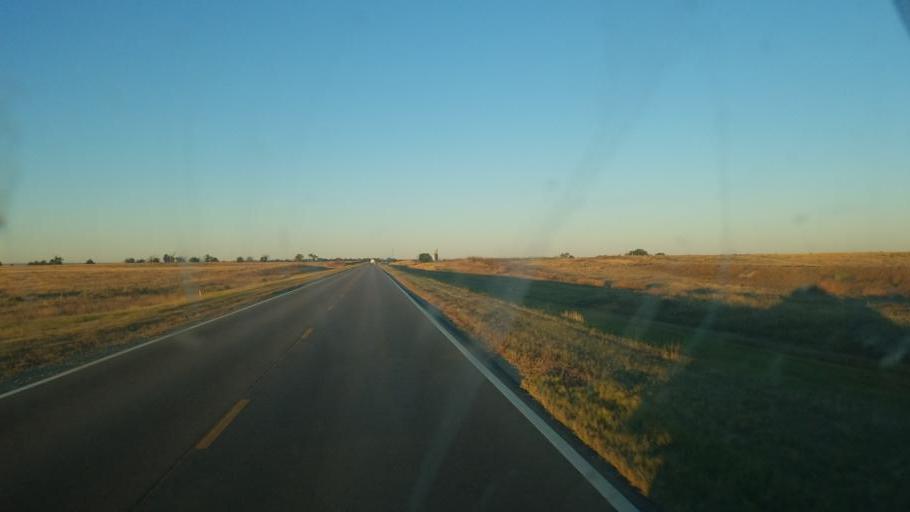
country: US
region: Kansas
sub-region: Wallace County
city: Sharon Springs
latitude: 38.8756
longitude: -101.9358
